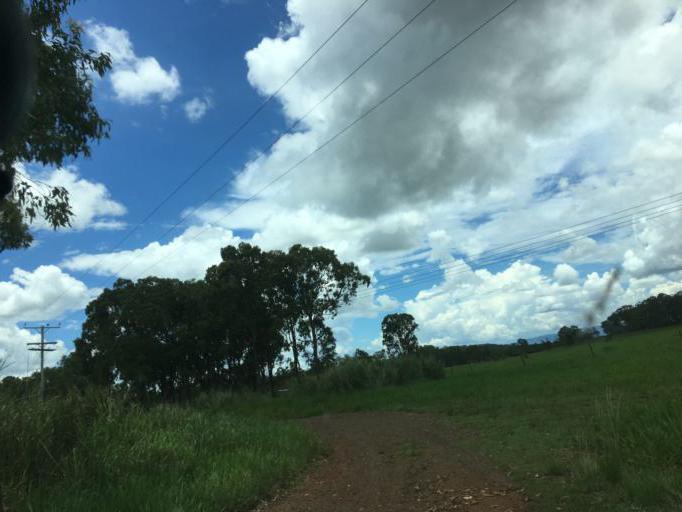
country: AU
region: Queensland
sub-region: Tablelands
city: Mareeba
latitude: -16.9904
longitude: 145.5238
